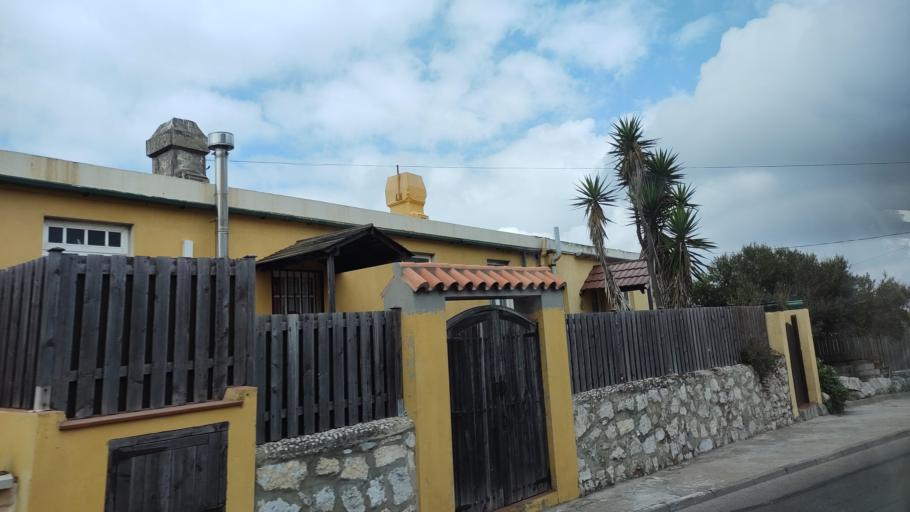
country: GI
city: Gibraltar
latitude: 36.1133
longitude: -5.3485
